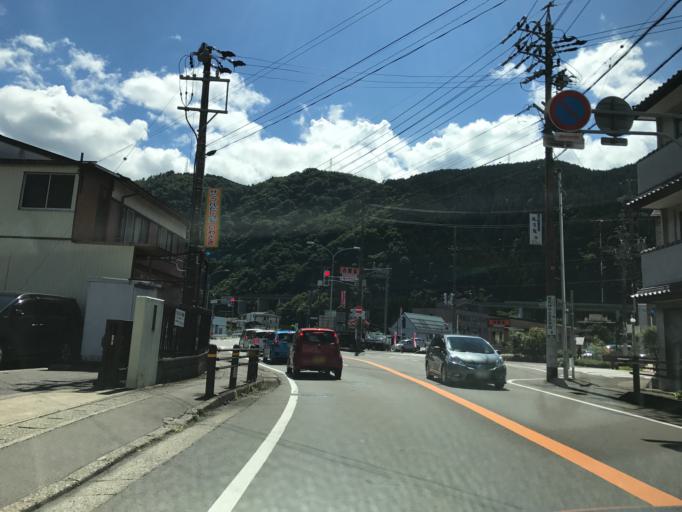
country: JP
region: Gifu
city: Gujo
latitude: 35.7445
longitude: 136.9490
